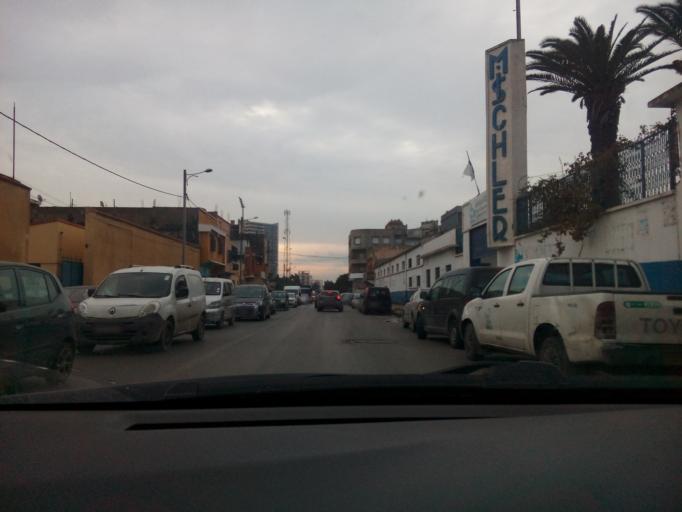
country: DZ
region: Oran
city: Oran
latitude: 35.6845
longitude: -0.6394
